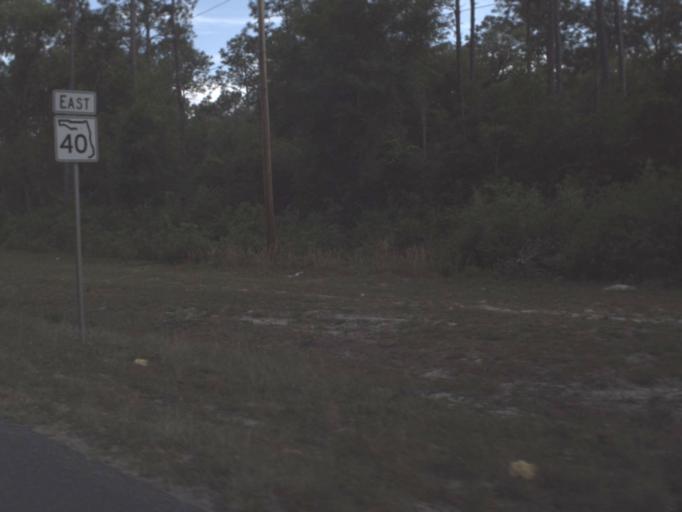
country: US
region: Florida
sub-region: Marion County
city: Silver Springs Shores
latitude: 29.1938
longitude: -81.9119
